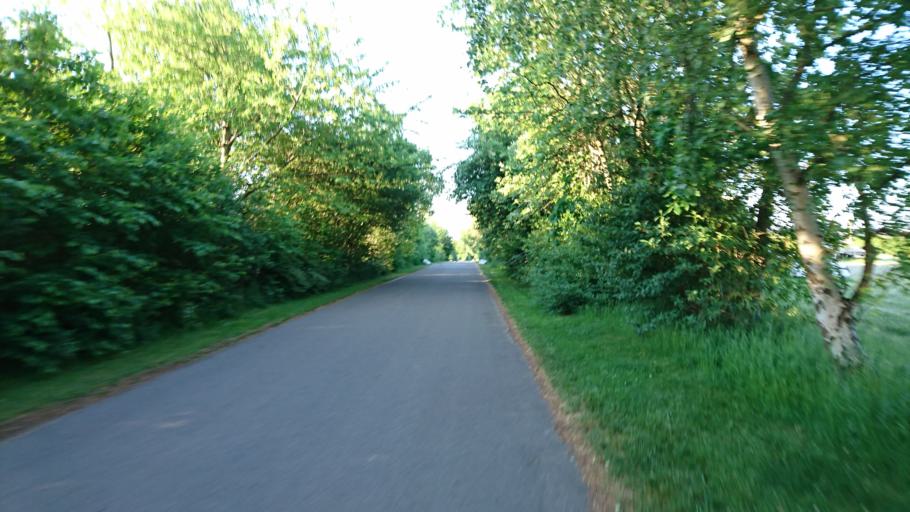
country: DK
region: Capital Region
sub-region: Ballerup Kommune
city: Ballerup
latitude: 55.7186
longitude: 12.3323
